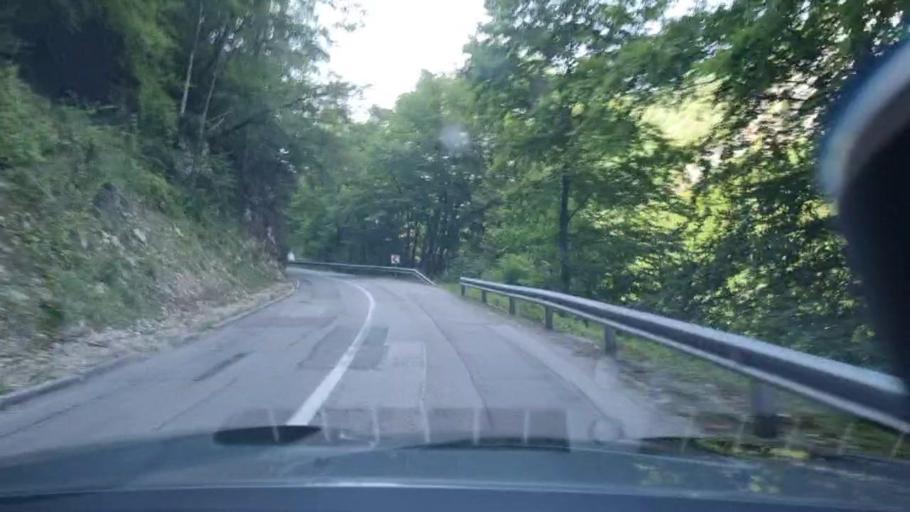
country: BA
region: Federation of Bosnia and Herzegovina
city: Stijena
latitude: 44.8863
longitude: 16.0584
